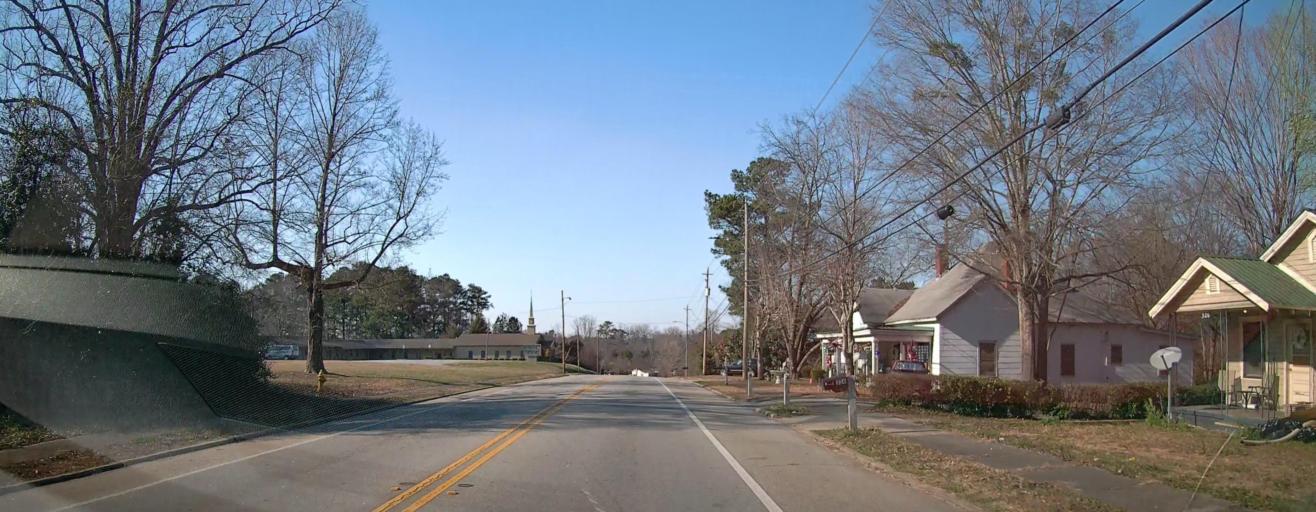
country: US
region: Georgia
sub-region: Butts County
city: Jackson
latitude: 33.2958
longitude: -83.9759
